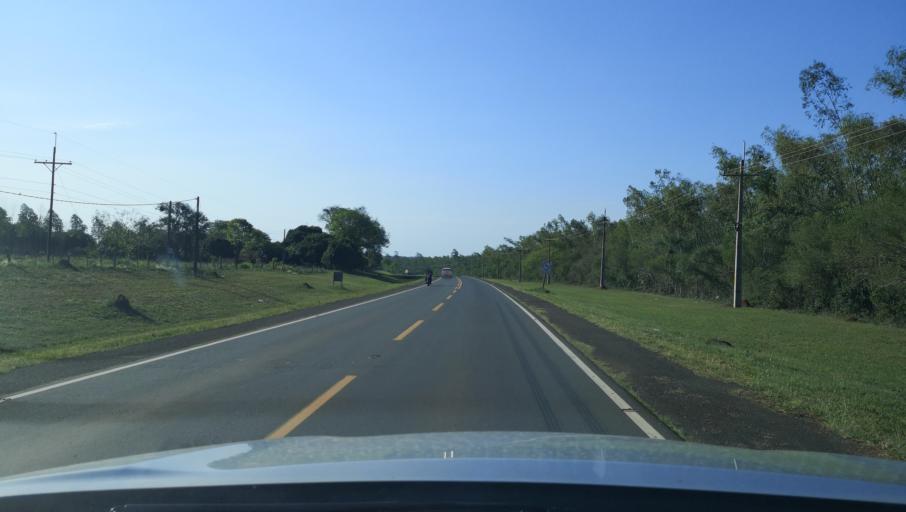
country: PY
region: Misiones
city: Santa Maria
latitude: -26.7614
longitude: -57.0336
